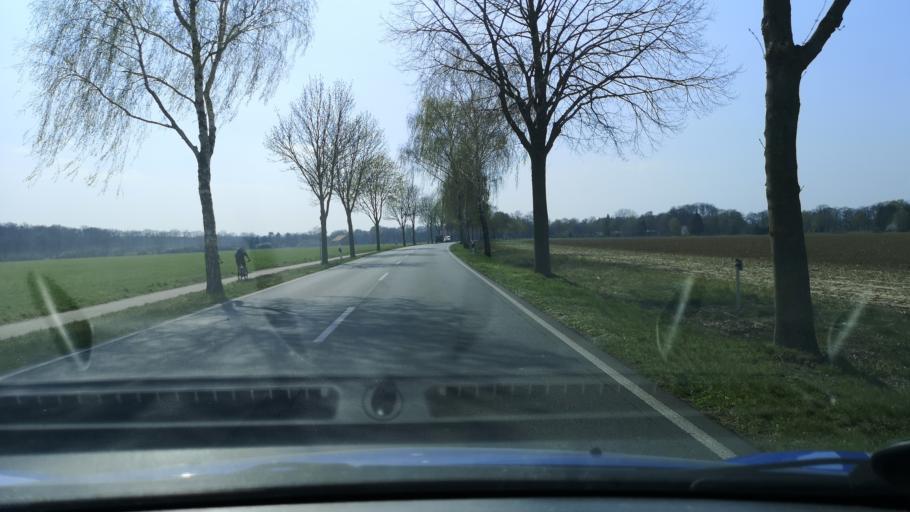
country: DE
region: Lower Saxony
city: Neustadt am Rubenberge
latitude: 52.5088
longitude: 9.5088
